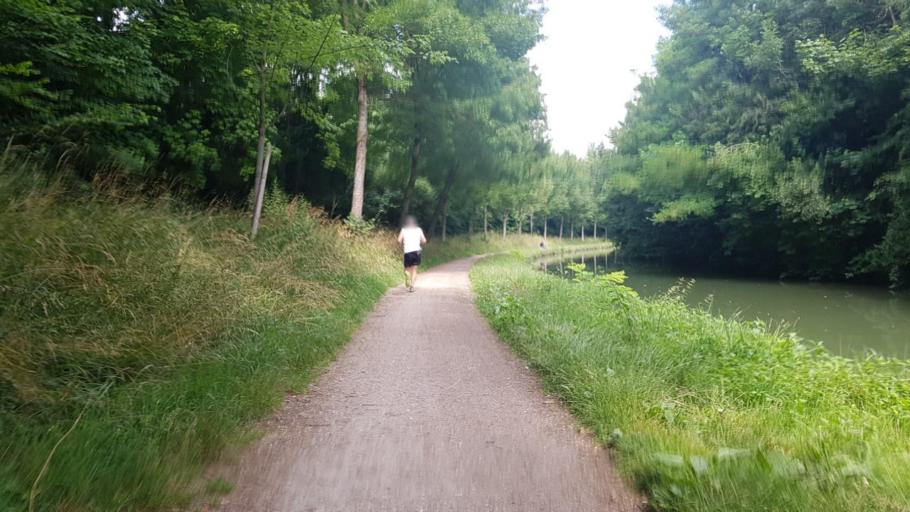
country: FR
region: Ile-de-France
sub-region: Departement de Seine-et-Marne
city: Claye-Souilly
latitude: 48.9526
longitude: 2.6784
